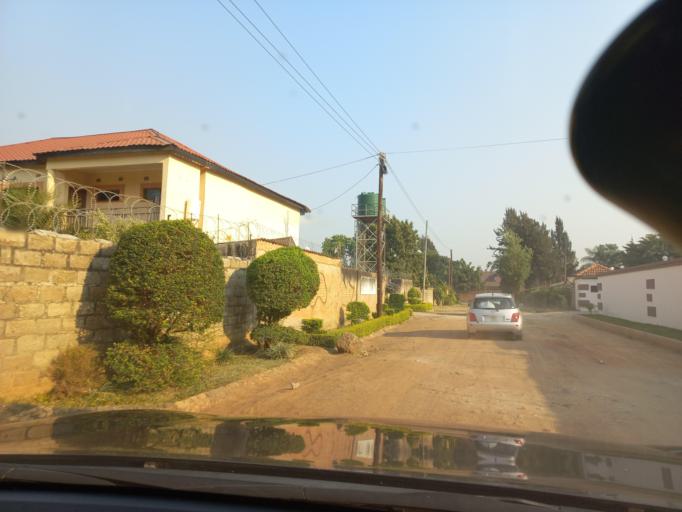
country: ZM
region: Lusaka
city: Lusaka
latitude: -15.4193
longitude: 28.3607
